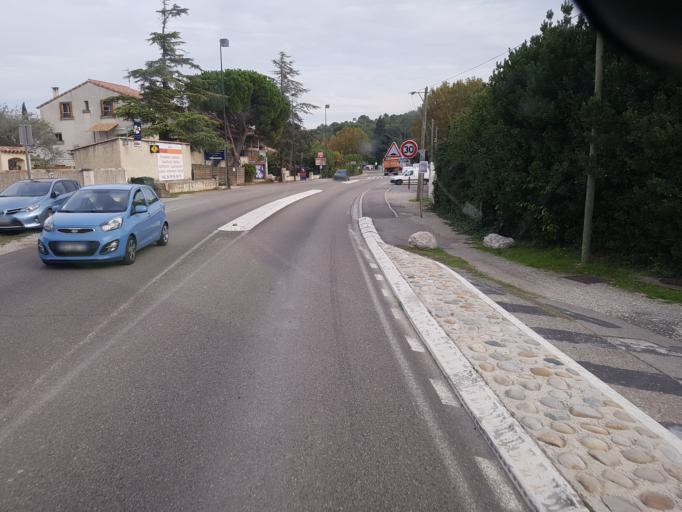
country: FR
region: Provence-Alpes-Cote d'Azur
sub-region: Departement des Bouches-du-Rhone
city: Barbentane
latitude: 43.9029
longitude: 4.7518
